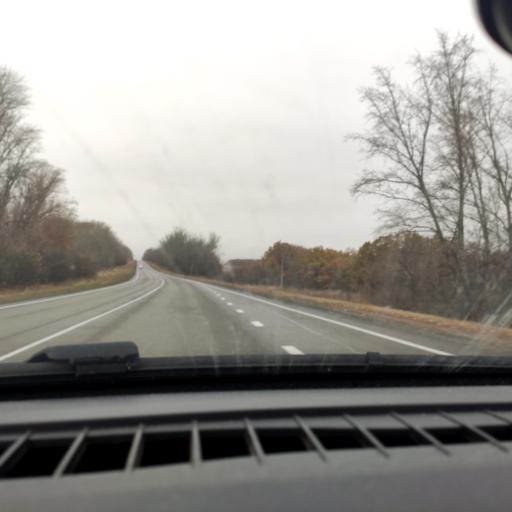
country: RU
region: Voronezj
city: Ostrogozhsk
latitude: 51.0059
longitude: 39.0003
